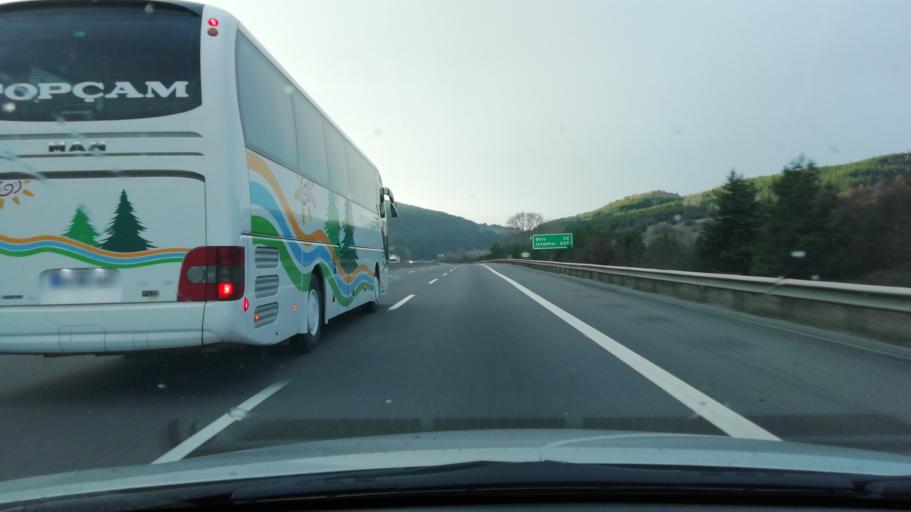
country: TR
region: Bolu
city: Bolu
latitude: 40.7374
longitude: 31.7972
